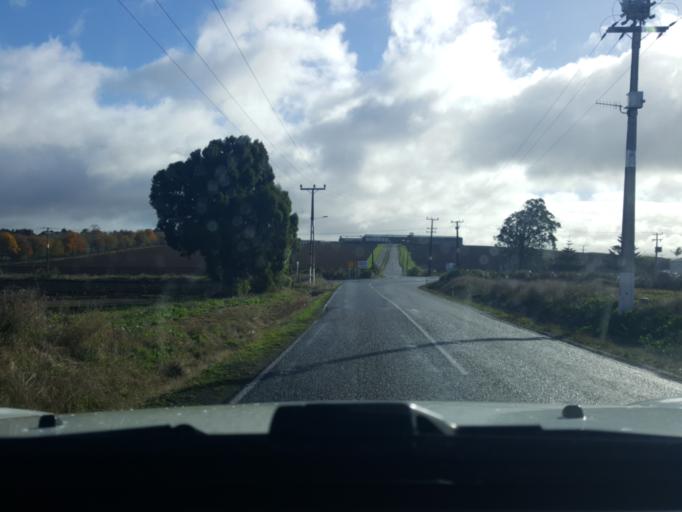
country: NZ
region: Auckland
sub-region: Auckland
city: Pukekohe East
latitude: -37.3111
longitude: 174.9872
